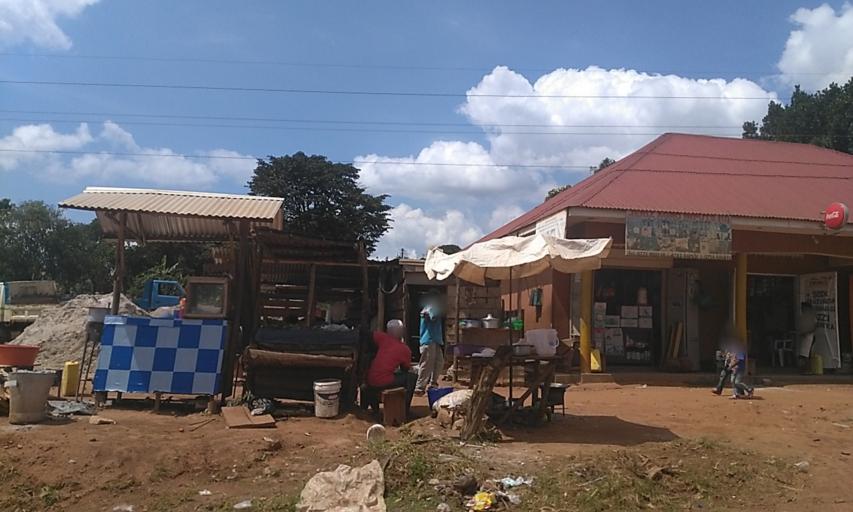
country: UG
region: Central Region
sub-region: Wakiso District
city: Wakiso
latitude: 0.3241
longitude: 32.4566
